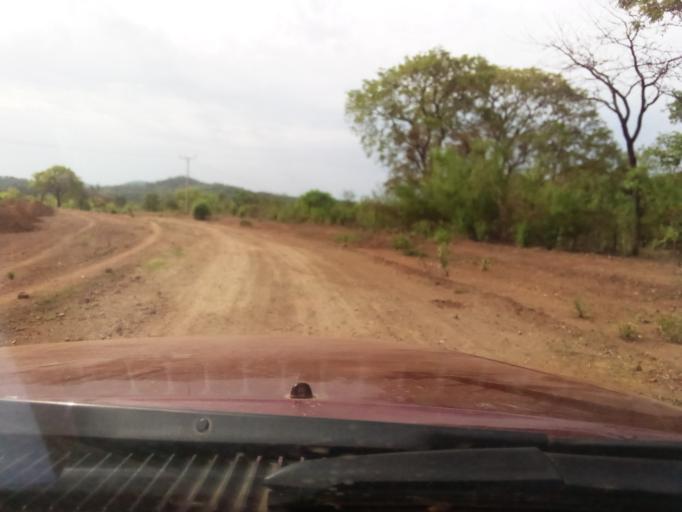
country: ET
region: Oromiya
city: Mendi
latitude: 10.0441
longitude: 35.3036
